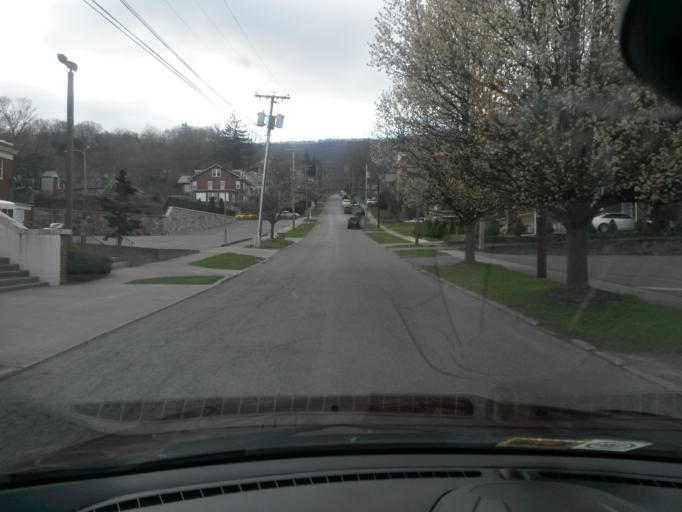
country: US
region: West Virginia
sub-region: Mercer County
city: Bluefield
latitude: 37.2549
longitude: -81.2194
